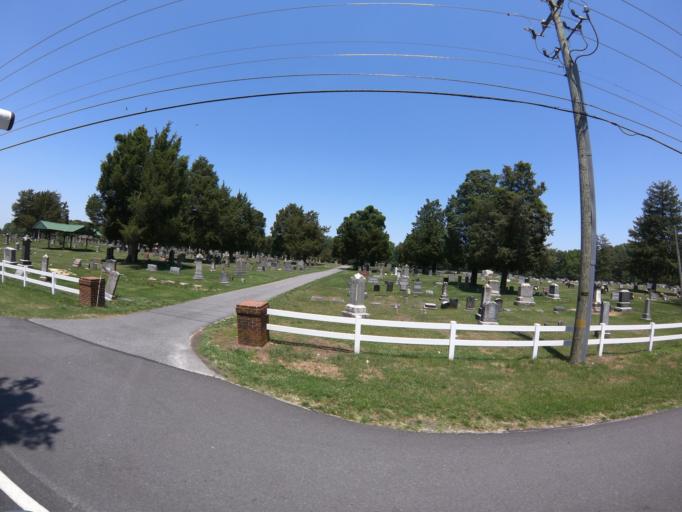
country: US
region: Delaware
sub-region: Kent County
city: Harrington
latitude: 38.9232
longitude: -75.5556
